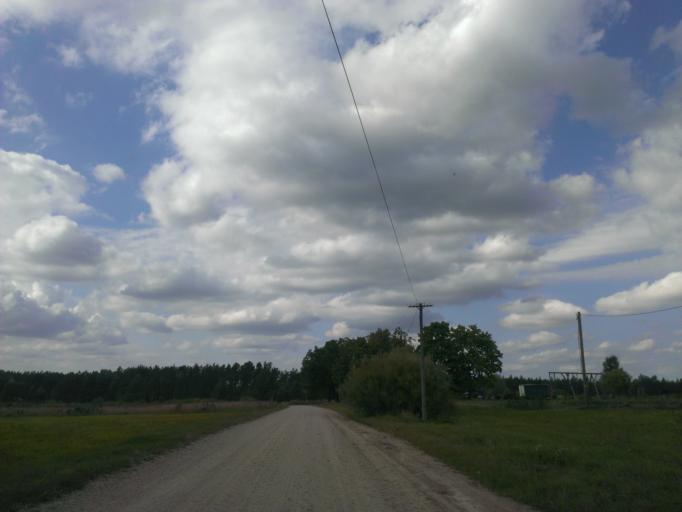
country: LV
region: Incukalns
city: Vangazi
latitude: 57.1191
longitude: 24.5706
